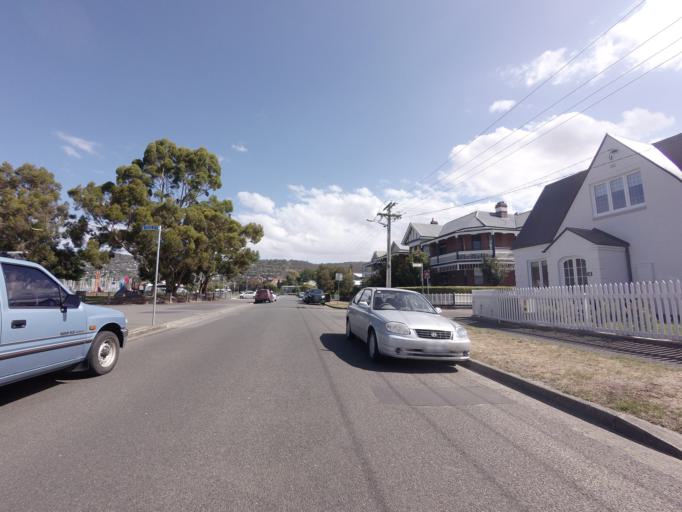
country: AU
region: Tasmania
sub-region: Hobart
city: Sandy Bay
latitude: -42.8954
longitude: 147.3329
